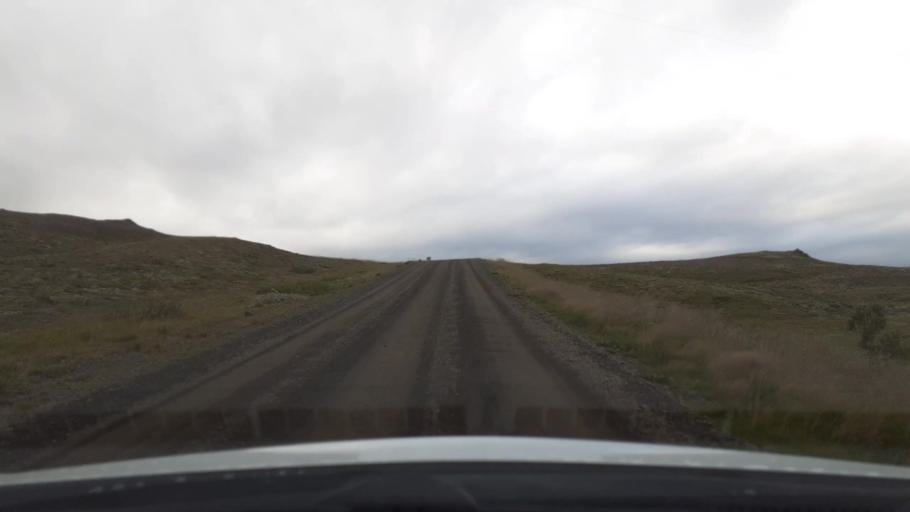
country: IS
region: Capital Region
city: Mosfellsbaer
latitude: 64.1998
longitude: -21.5582
